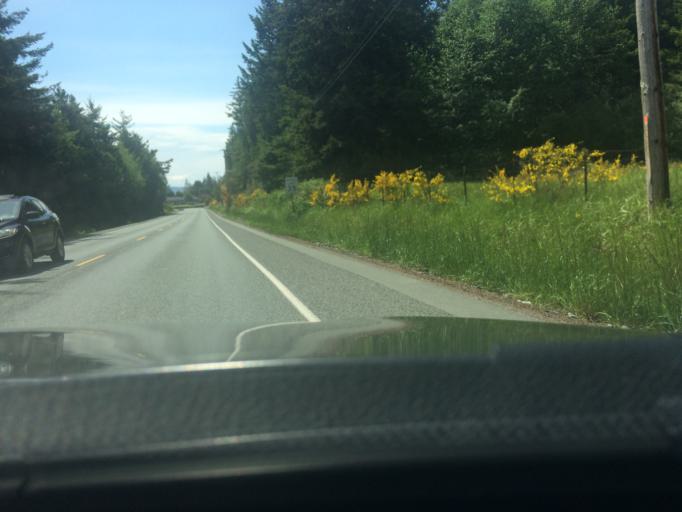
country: US
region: Washington
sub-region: Island County
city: Ault Field
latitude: 48.4264
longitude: -122.6647
